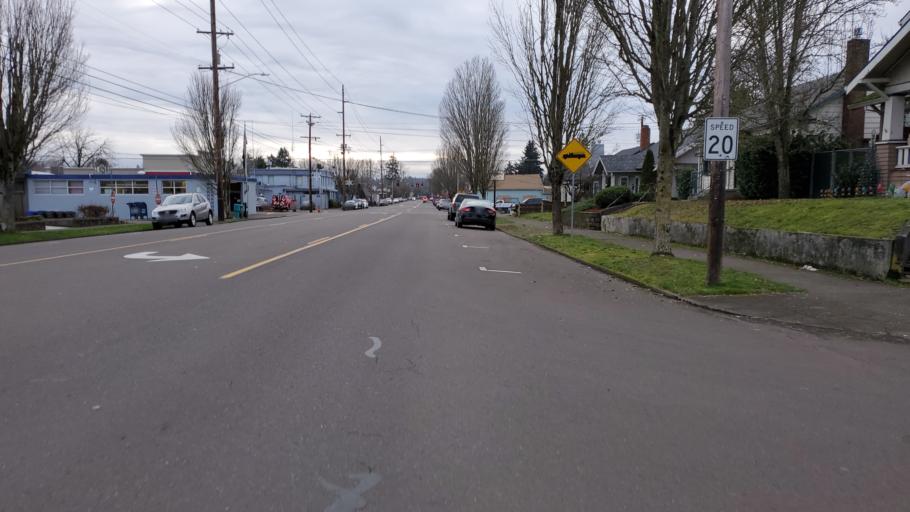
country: US
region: Oregon
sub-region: Clackamas County
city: Gladstone
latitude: 45.3815
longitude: -122.5955
